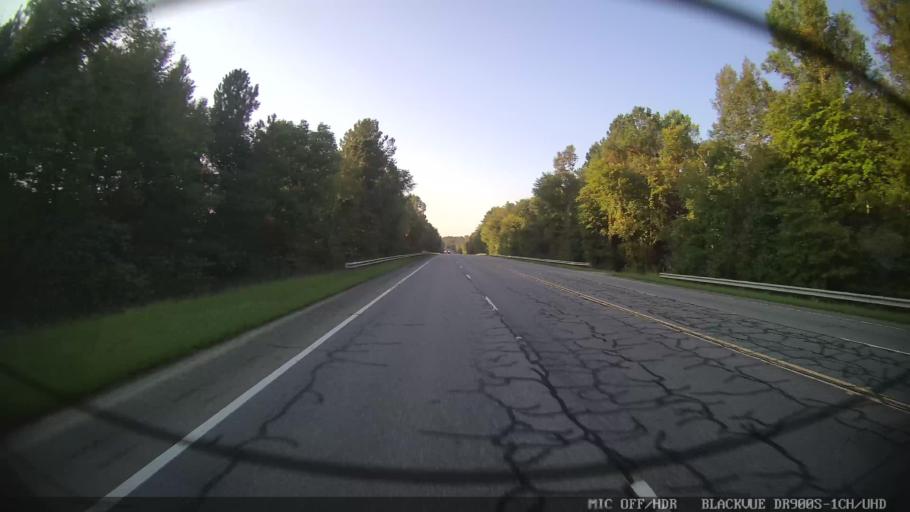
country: US
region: Georgia
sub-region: Murray County
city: Chatsworth
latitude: 34.7057
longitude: -84.7426
